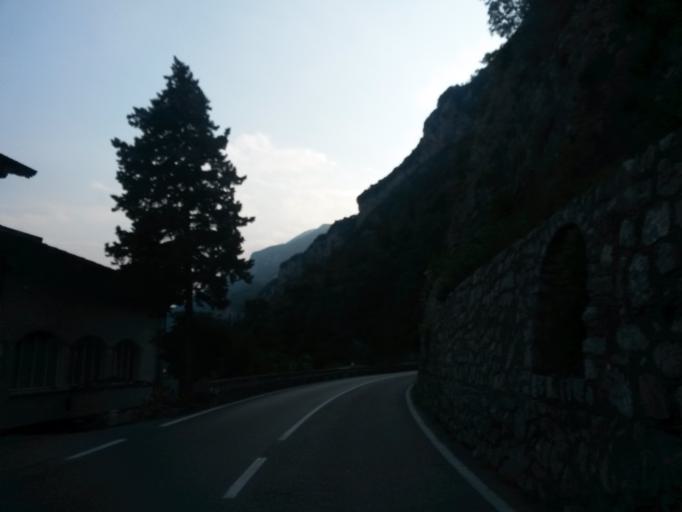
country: IT
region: Lombardy
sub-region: Provincia di Brescia
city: Gardola
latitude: 45.7358
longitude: 10.7341
